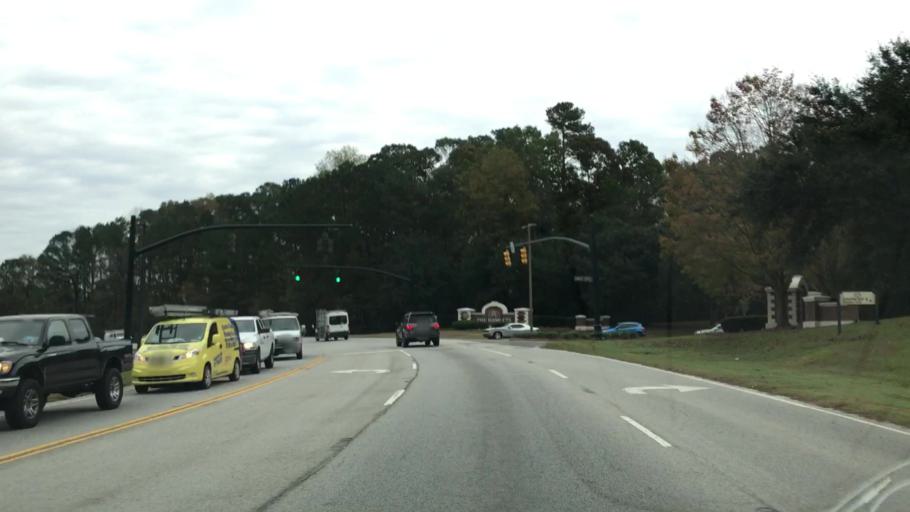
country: US
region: South Carolina
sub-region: Berkeley County
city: Ladson
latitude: 33.0157
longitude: -80.0808
